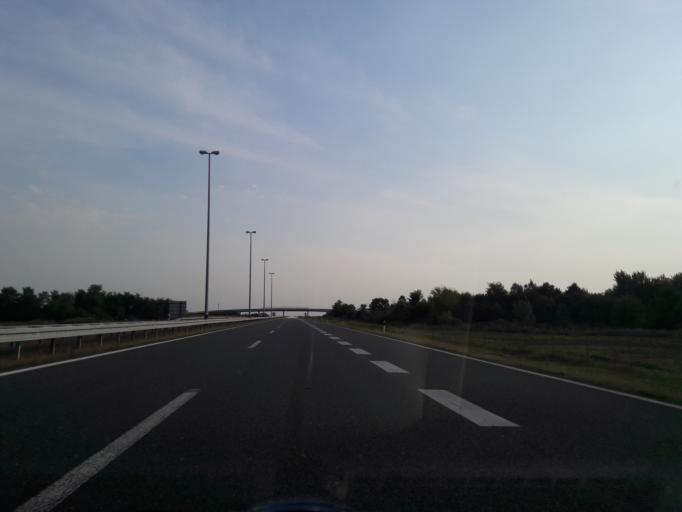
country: HR
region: Osjecko-Baranjska
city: Piskorevci
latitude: 45.2691
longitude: 18.3461
